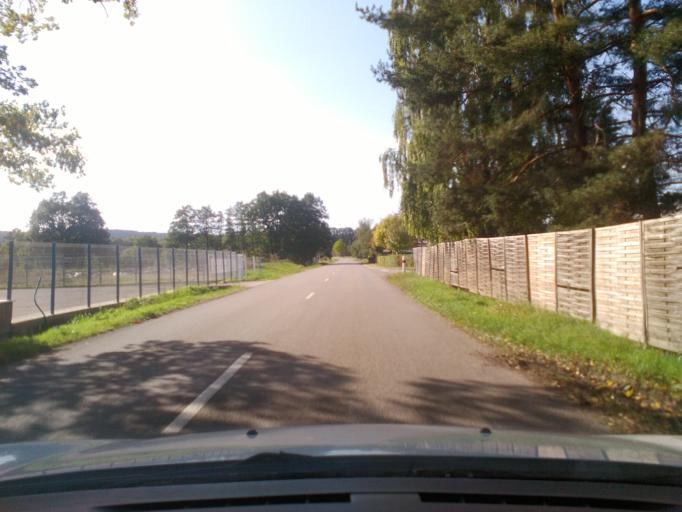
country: FR
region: Lorraine
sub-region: Departement des Vosges
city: Sainte-Marguerite
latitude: 48.2671
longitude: 6.9975
